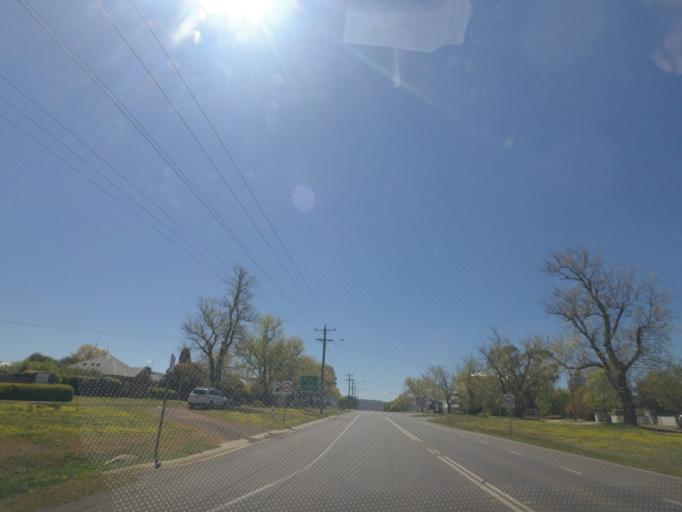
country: AU
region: Victoria
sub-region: Hume
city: Sunbury
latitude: -37.2789
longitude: 144.7367
